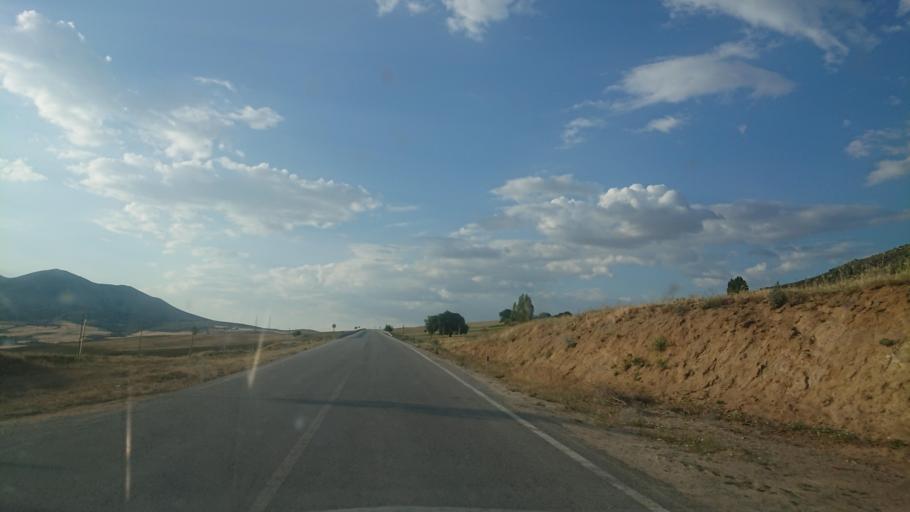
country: TR
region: Aksaray
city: Balci
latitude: 38.5923
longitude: 34.1019
